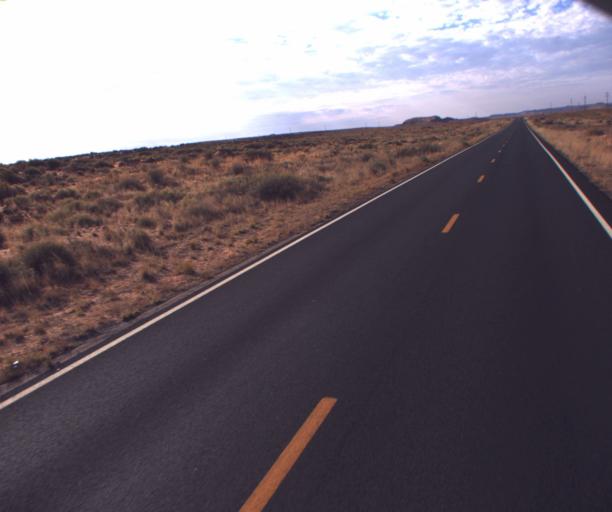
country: US
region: Arizona
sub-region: Apache County
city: Many Farms
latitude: 36.8020
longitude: -109.6486
